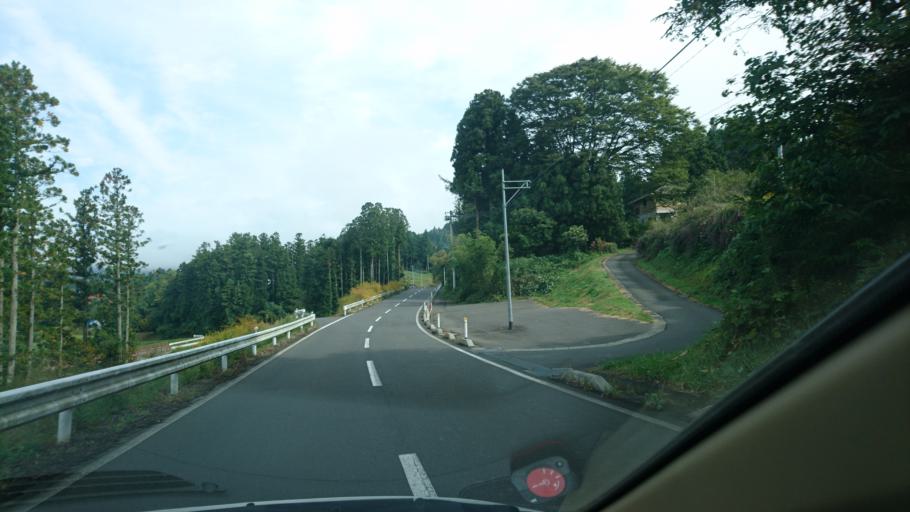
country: JP
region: Iwate
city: Ichinoseki
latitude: 38.9561
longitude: 141.1716
